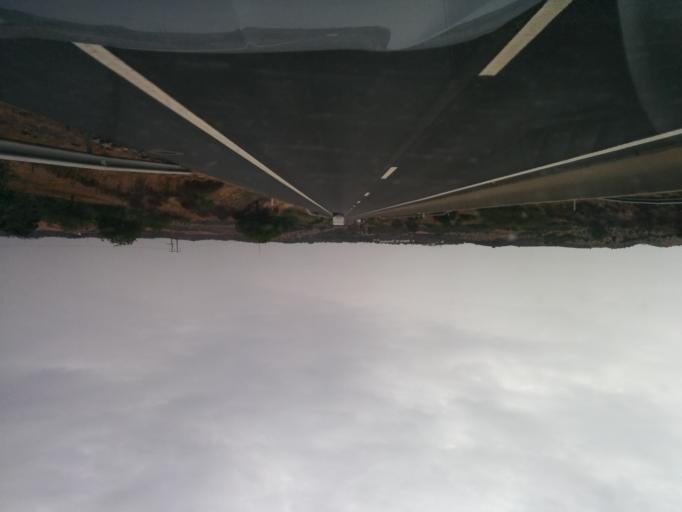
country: PT
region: Faro
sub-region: Castro Marim
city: Castro Marim
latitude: 37.2147
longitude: -7.4830
